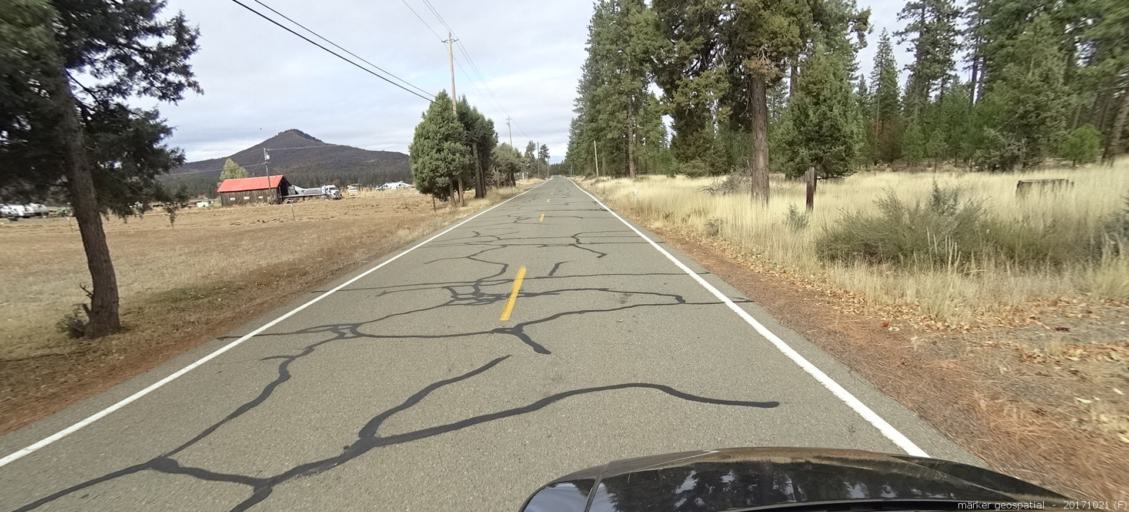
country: US
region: California
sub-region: Shasta County
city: Burney
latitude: 40.9159
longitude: -121.6469
